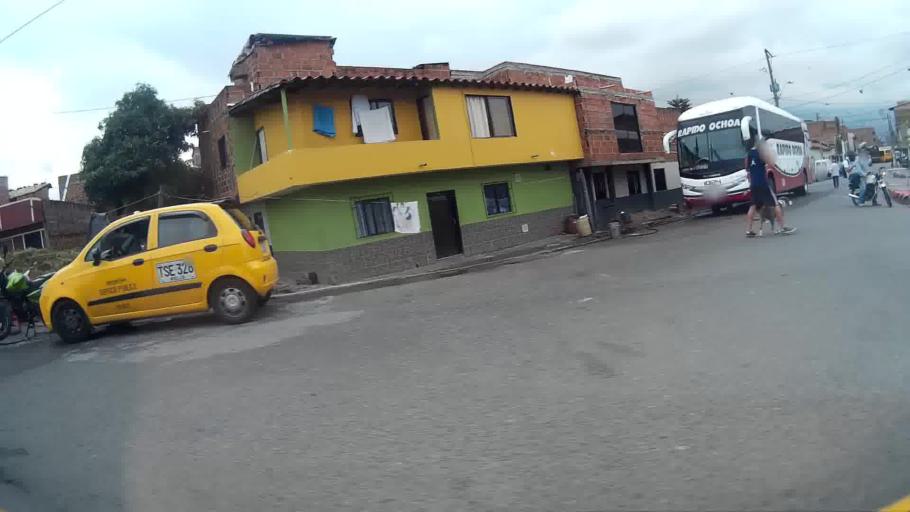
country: CO
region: Antioquia
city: Medellin
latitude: 6.2265
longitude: -75.5874
